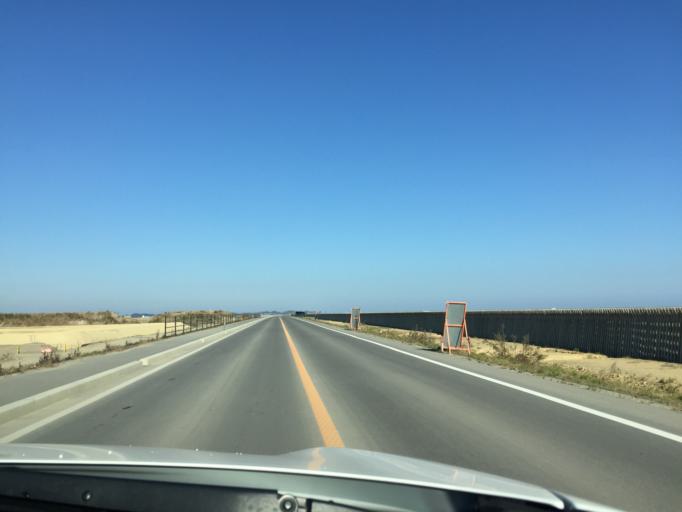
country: JP
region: Miyagi
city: Marumori
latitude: 37.7815
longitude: 140.9842
